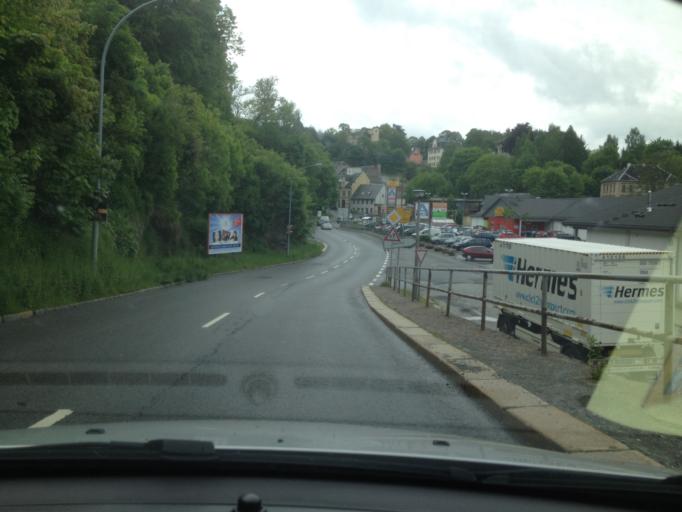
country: DE
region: Saxony
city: Annaberg-Buchholz
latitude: 50.5781
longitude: 12.9993
